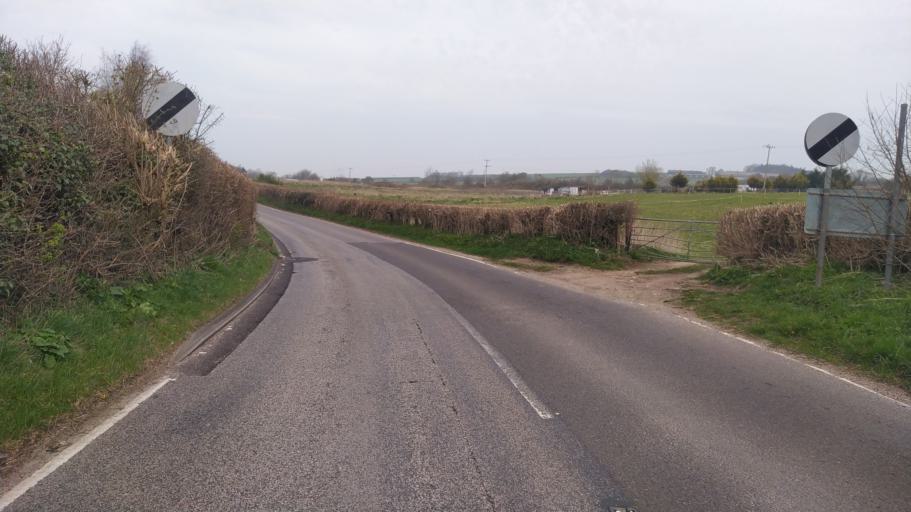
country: GB
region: England
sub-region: Dorset
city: Dorchester
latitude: 50.7577
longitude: -2.5405
